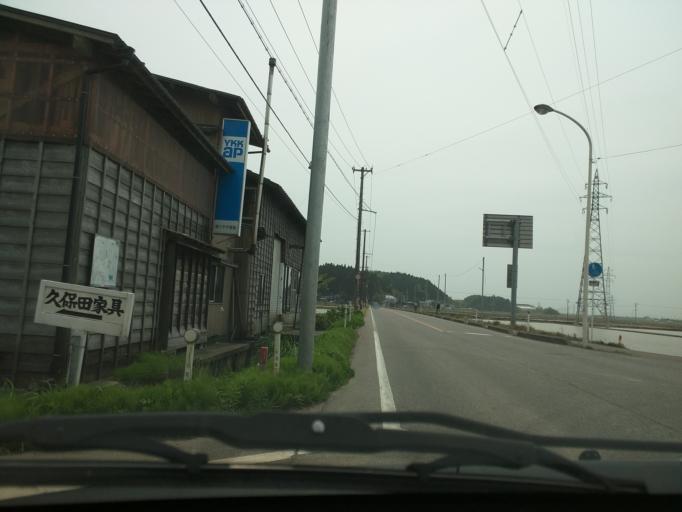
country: JP
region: Niigata
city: Mitsuke
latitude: 37.5705
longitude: 138.9387
